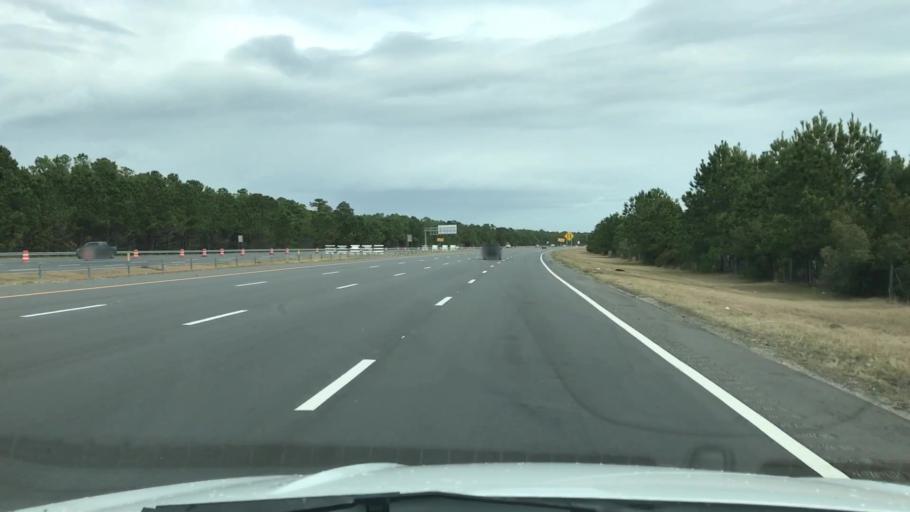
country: US
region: South Carolina
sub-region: Horry County
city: Socastee
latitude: 33.7075
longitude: -79.0105
